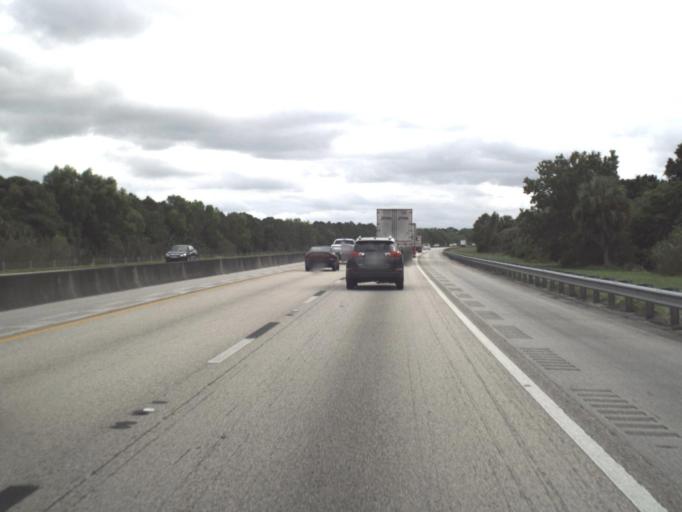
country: US
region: Florida
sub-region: Palm Beach County
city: Palm Beach Gardens
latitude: 26.8794
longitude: -80.1299
